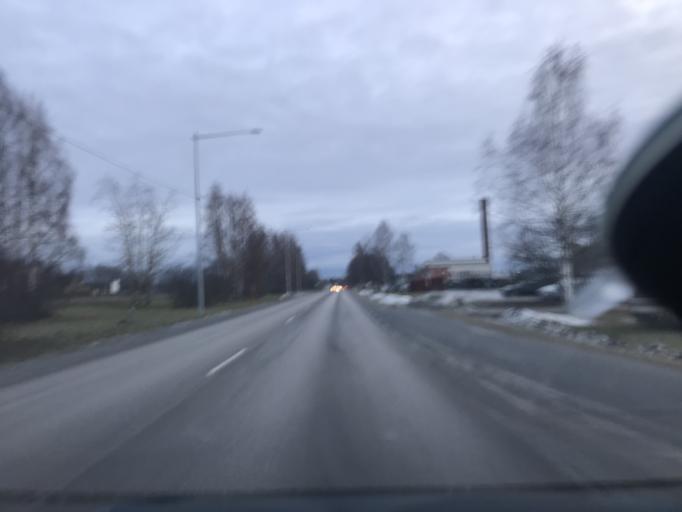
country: SE
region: Norrbotten
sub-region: Lulea Kommun
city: Gammelstad
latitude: 65.6450
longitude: 22.0055
